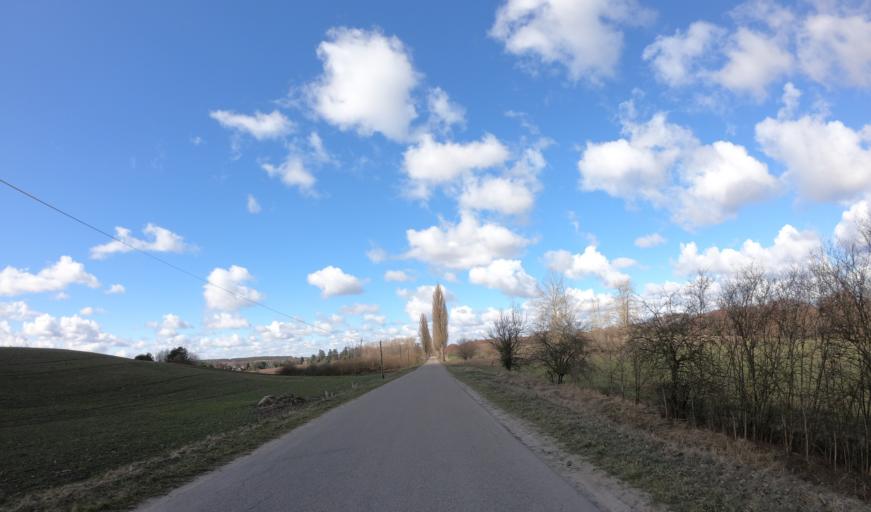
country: PL
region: West Pomeranian Voivodeship
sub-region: Powiat drawski
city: Drawsko Pomorskie
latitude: 53.4857
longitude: 15.8741
